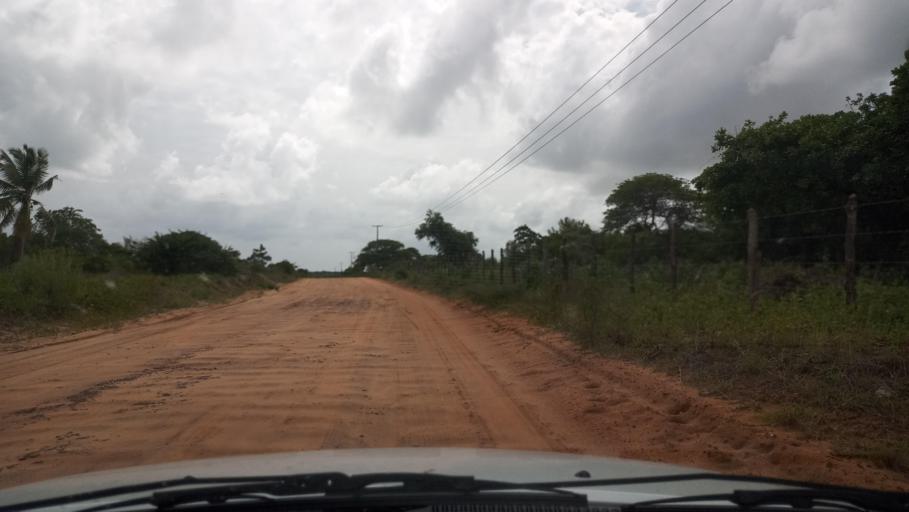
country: BR
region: Rio Grande do Norte
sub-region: Maxaranguape
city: Sao Miguel
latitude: -5.4843
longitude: -35.3112
